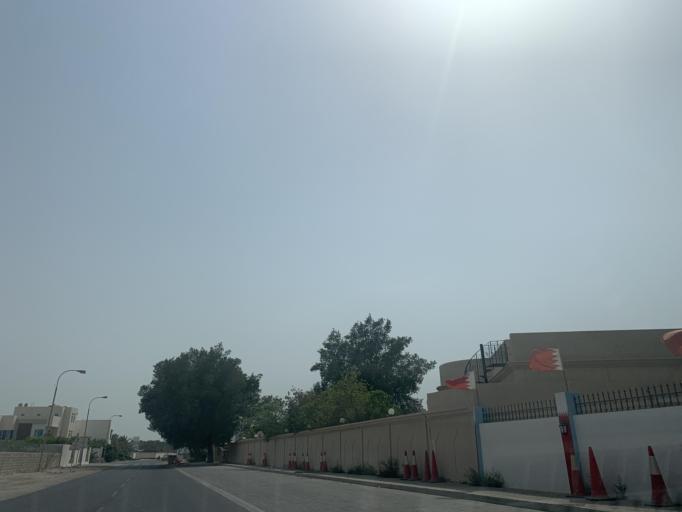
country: BH
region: Manama
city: Jidd Hafs
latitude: 26.1998
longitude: 50.4707
